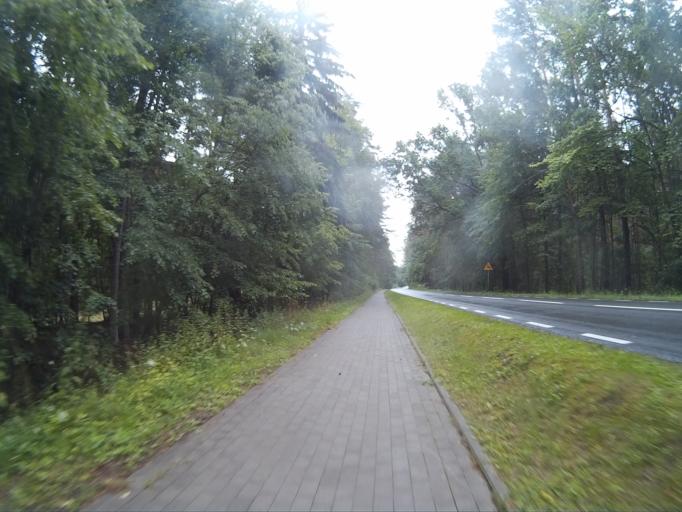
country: PL
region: Kujawsko-Pomorskie
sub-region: Powiat swiecki
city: Osie
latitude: 53.6124
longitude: 18.2929
